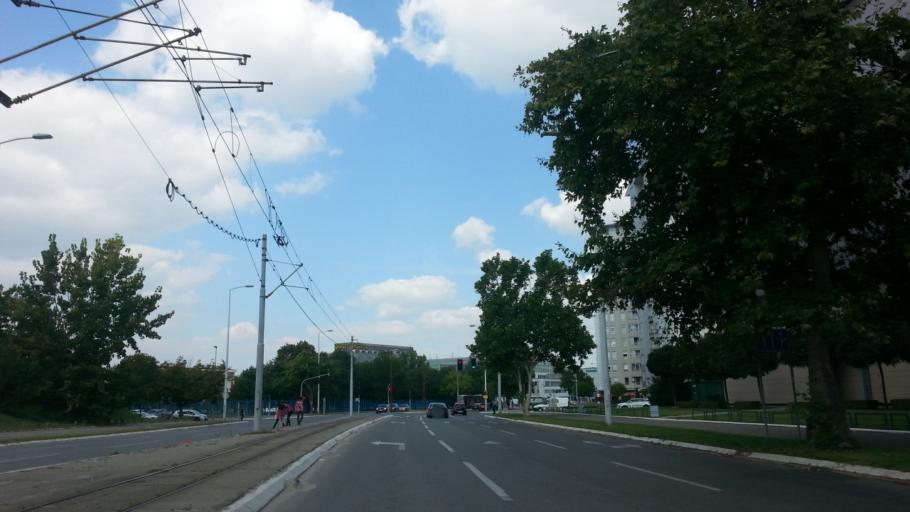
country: RS
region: Central Serbia
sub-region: Belgrade
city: Novi Beograd
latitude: 44.8054
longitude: 20.4038
